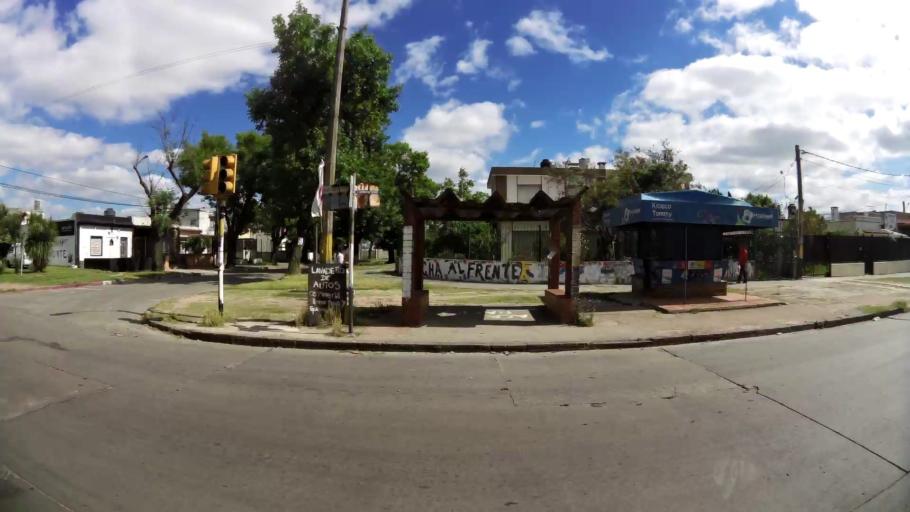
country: UY
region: Canelones
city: Paso de Carrasco
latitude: -34.8723
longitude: -56.1213
